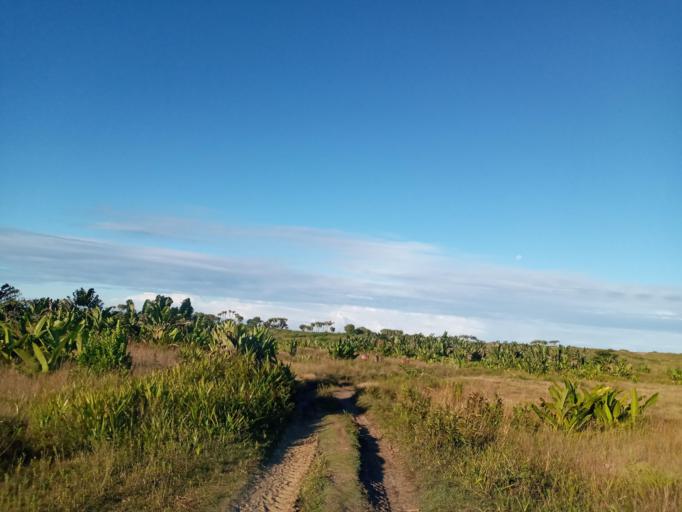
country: MG
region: Anosy
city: Fort Dauphin
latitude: -24.4314
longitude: 47.3015
